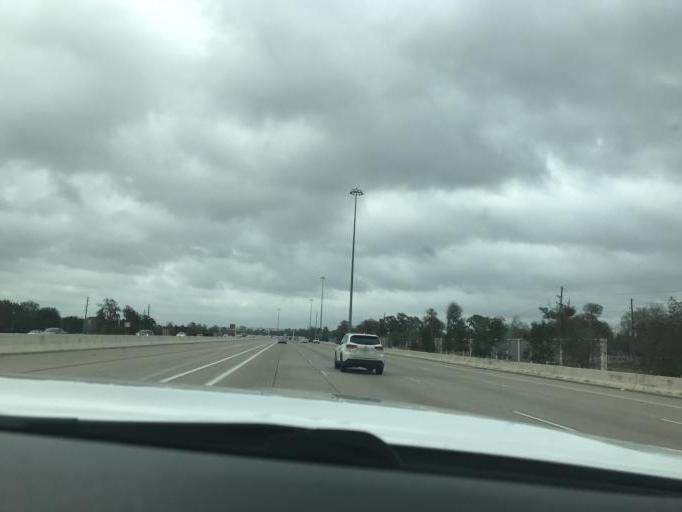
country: US
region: Texas
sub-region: Fort Bend County
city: Greatwood
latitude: 29.5630
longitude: -95.6821
